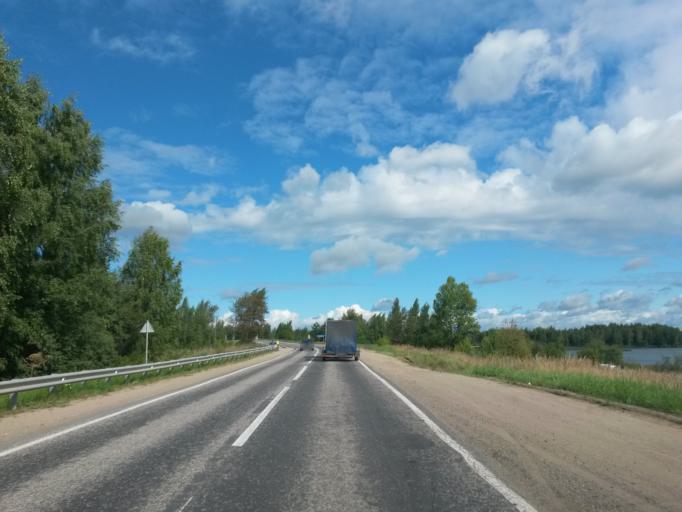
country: RU
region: Jaroslavl
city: Yaroslavl
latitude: 57.5122
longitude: 39.8971
